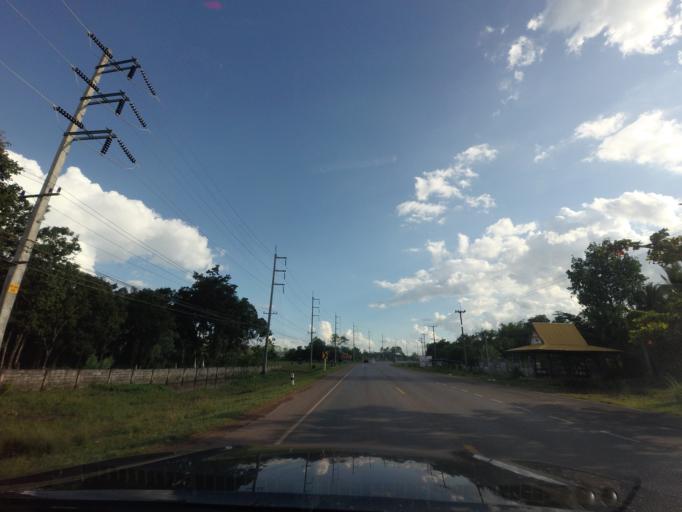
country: TH
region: Changwat Udon Thani
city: Thung Fon
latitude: 17.5022
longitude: 103.2035
